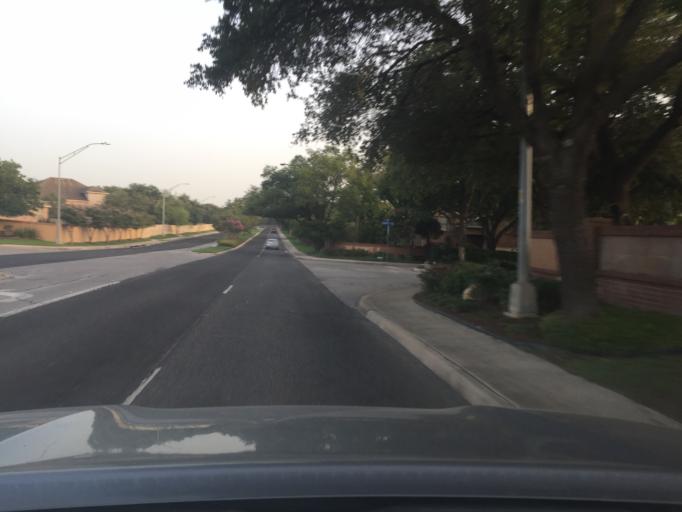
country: US
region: Texas
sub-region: Bexar County
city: Hollywood Park
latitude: 29.6517
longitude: -98.4950
